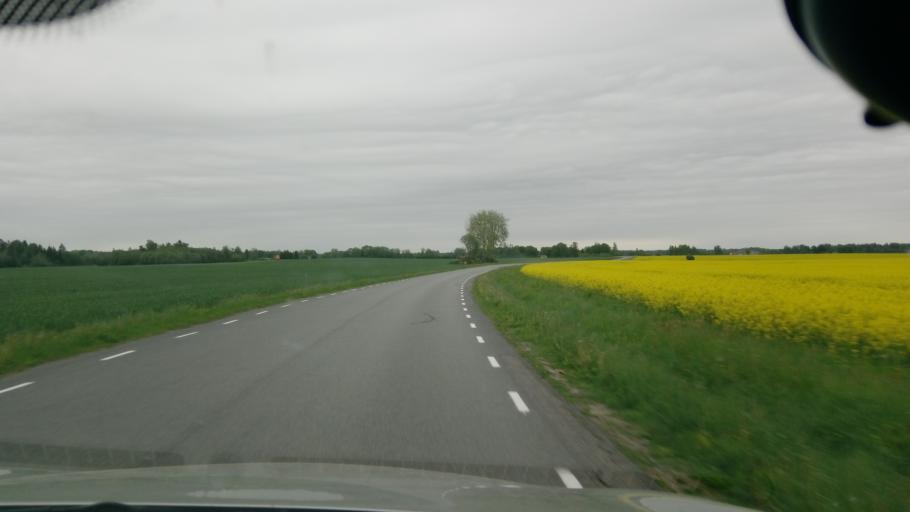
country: EE
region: Jaervamaa
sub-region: Koeru vald
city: Koeru
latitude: 58.9971
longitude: 26.0649
